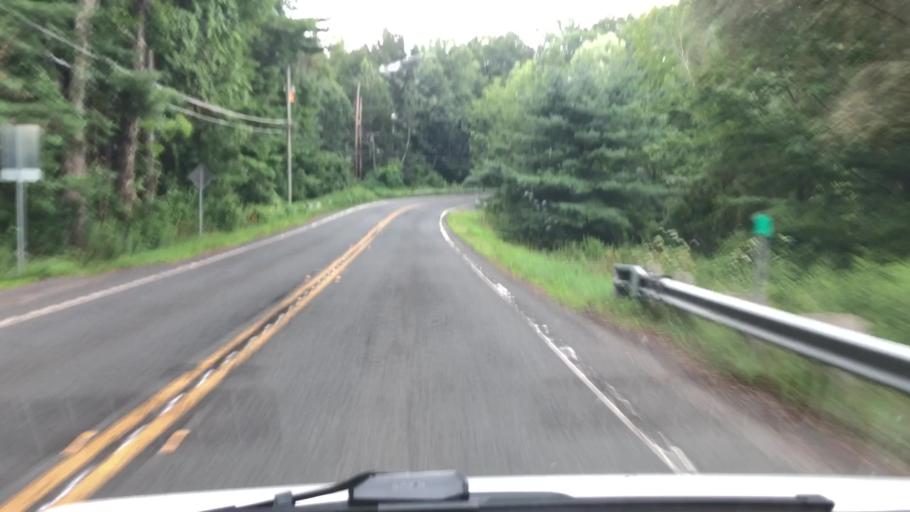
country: US
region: Massachusetts
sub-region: Franklin County
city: Conway
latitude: 42.5119
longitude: -72.6703
